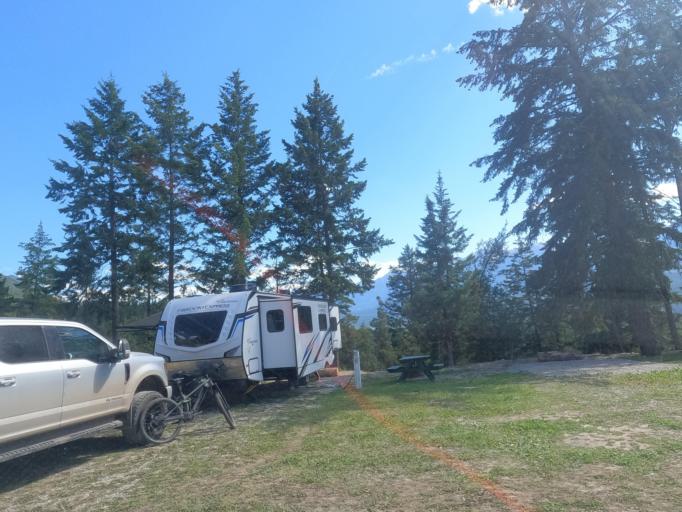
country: CA
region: British Columbia
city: Golden
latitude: 51.3002
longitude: -116.9478
